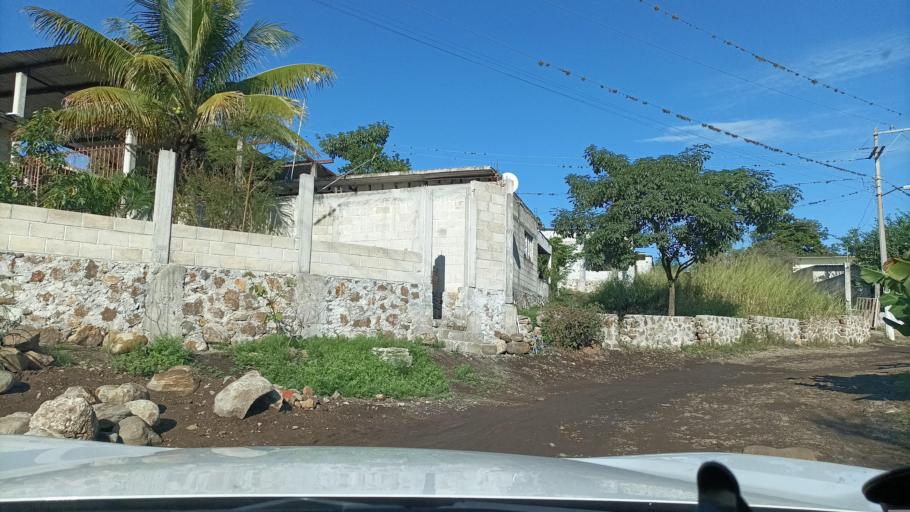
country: MX
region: Veracruz
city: Paso del Macho
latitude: 18.9758
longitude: -96.7304
